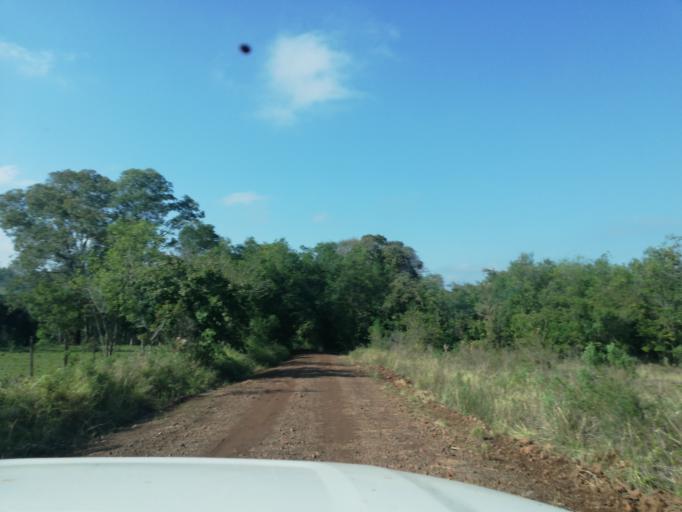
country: AR
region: Misiones
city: Cerro Azul
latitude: -27.6226
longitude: -55.5266
